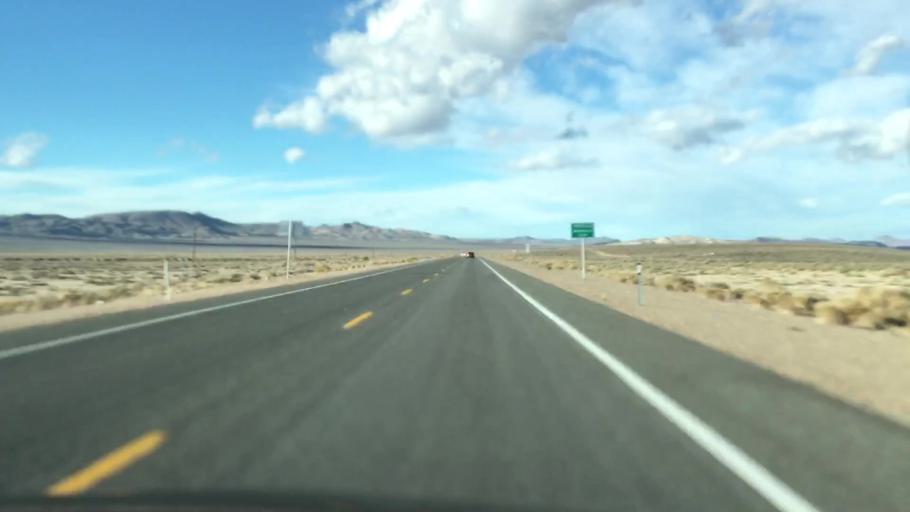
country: US
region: Nevada
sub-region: Esmeralda County
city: Goldfield
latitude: 37.4564
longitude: -117.1708
